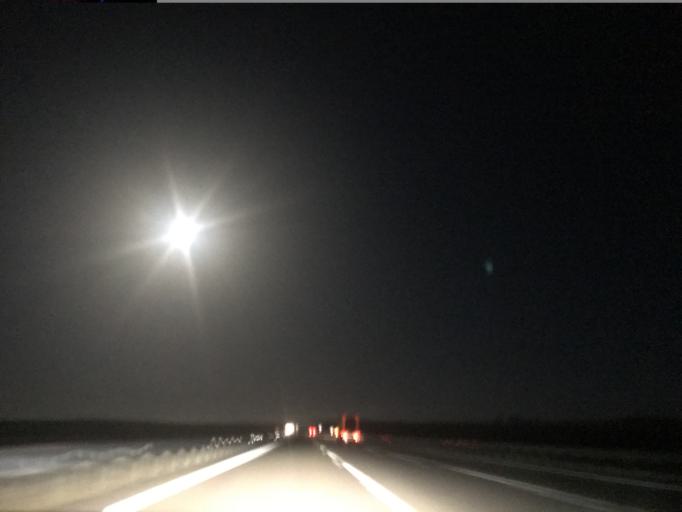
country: TR
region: Nigde
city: Ulukisla
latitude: 37.6381
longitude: 34.3964
